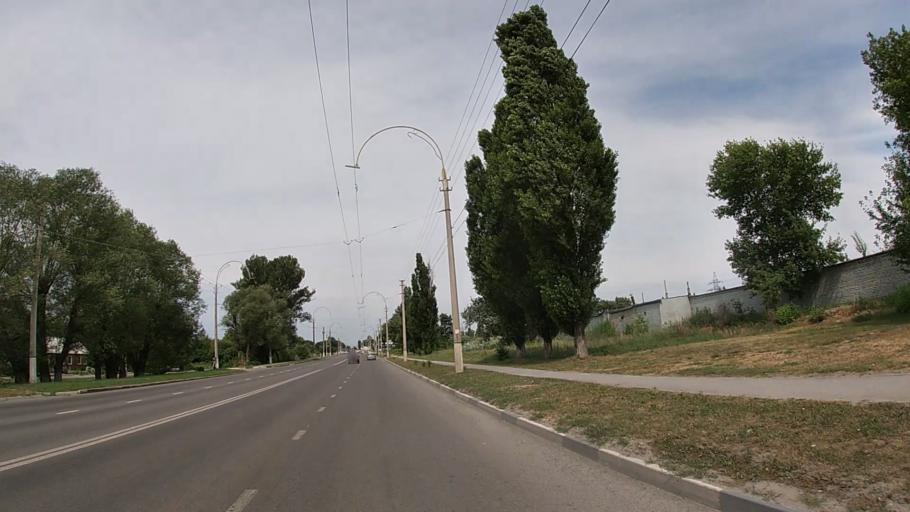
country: RU
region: Belgorod
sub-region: Belgorodskiy Rayon
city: Belgorod
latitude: 50.6107
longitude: 36.5422
